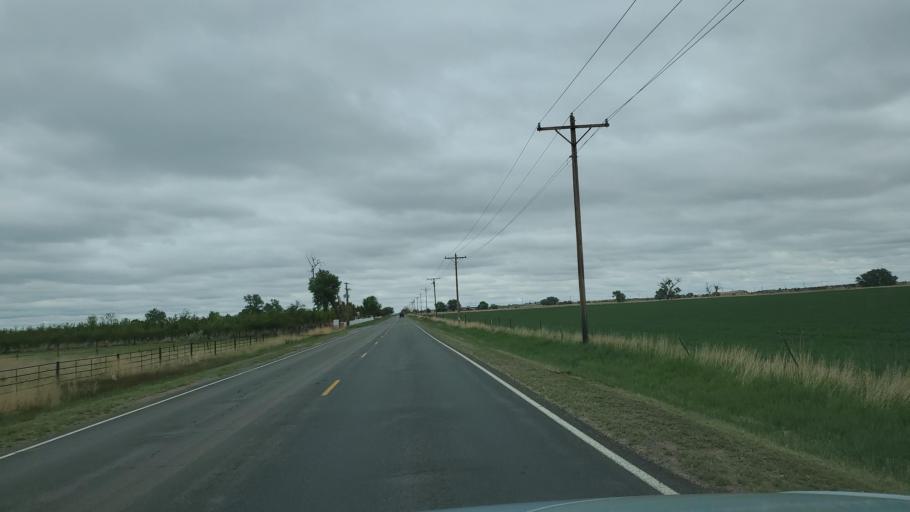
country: US
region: Colorado
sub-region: Weld County
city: Lochbuie
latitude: 39.9724
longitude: -104.7204
